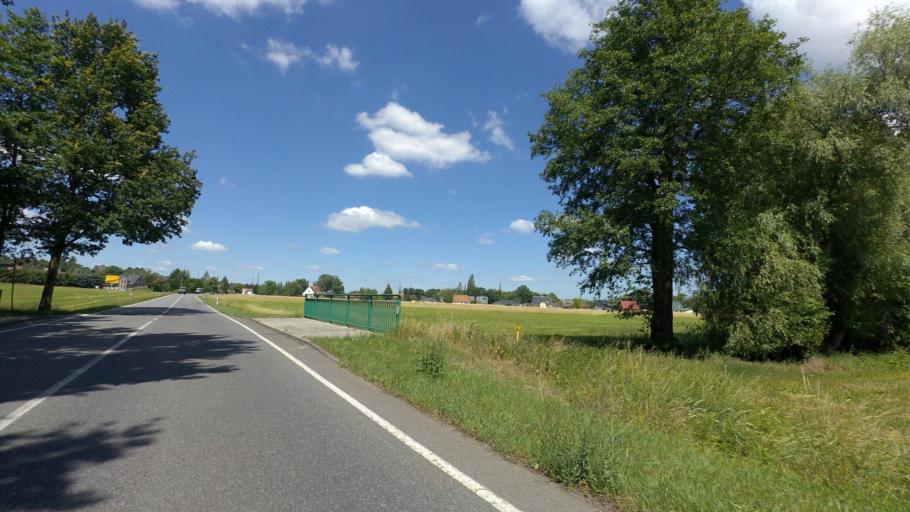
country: DE
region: Brandenburg
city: Luckau
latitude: 51.8745
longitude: 13.6973
